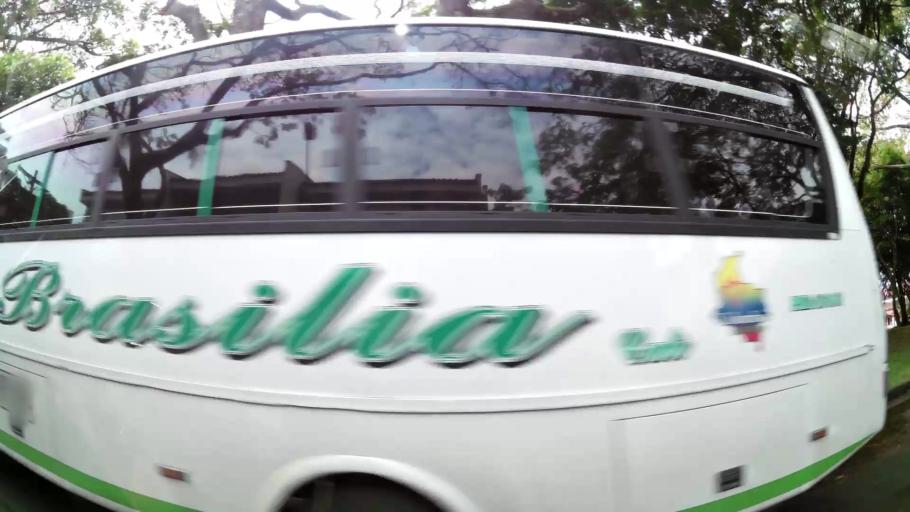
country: CO
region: Valle del Cauca
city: Cali
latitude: 3.3898
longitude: -76.5437
